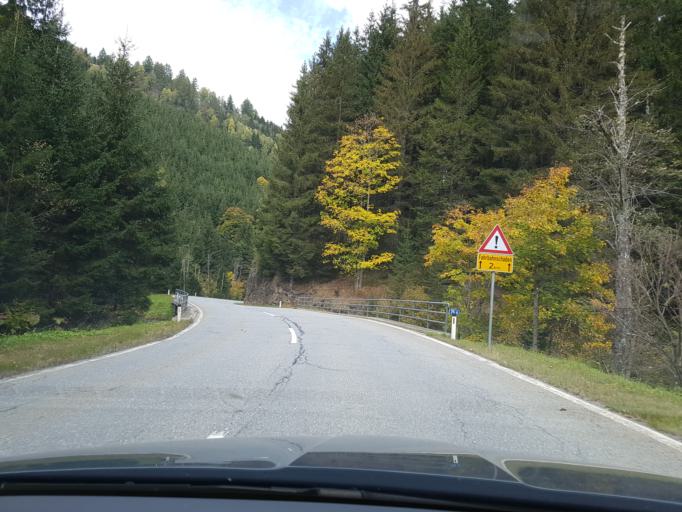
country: AT
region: Salzburg
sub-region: Politischer Bezirk Tamsweg
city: Ramingstein
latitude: 47.0255
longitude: 13.9007
